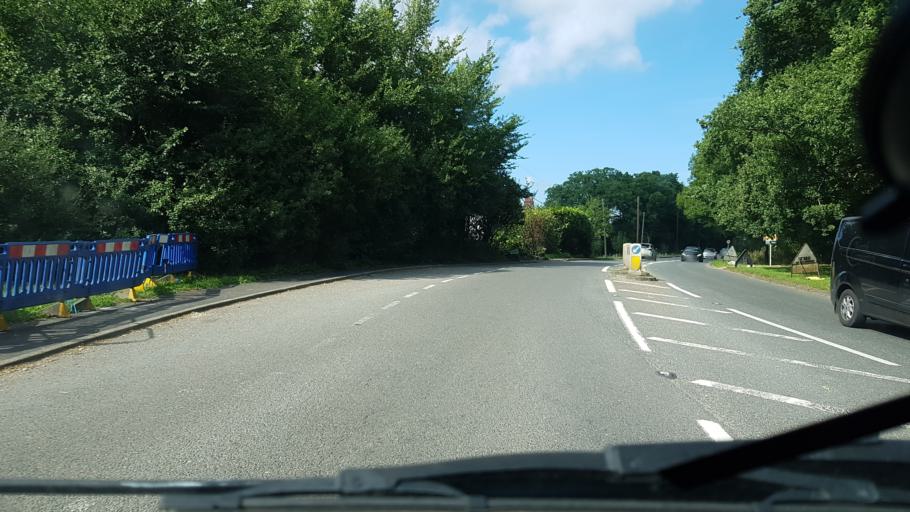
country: GB
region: England
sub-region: Surrey
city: Cranleigh
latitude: 51.1081
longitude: -0.5151
